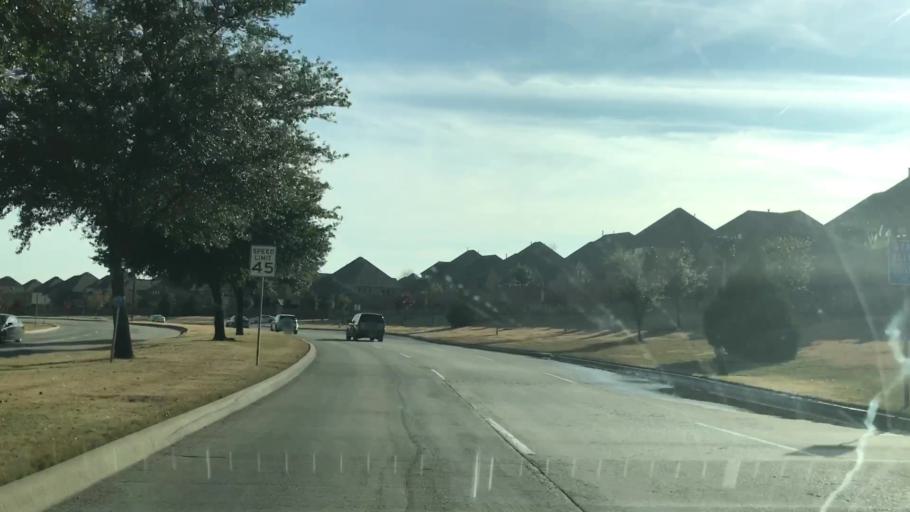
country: US
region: Texas
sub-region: Dallas County
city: Farmers Branch
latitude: 32.9092
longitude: -96.9453
